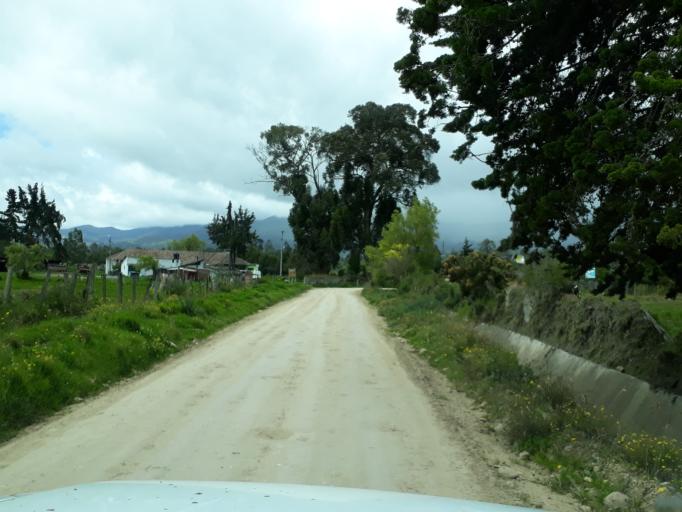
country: CO
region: Cundinamarca
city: Guasca
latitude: 4.8507
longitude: -73.9048
